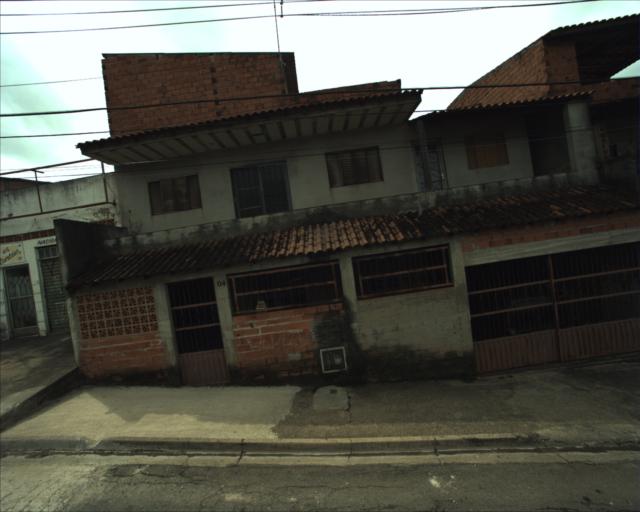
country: BR
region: Sao Paulo
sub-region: Sorocaba
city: Sorocaba
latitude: -23.4363
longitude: -47.5105
